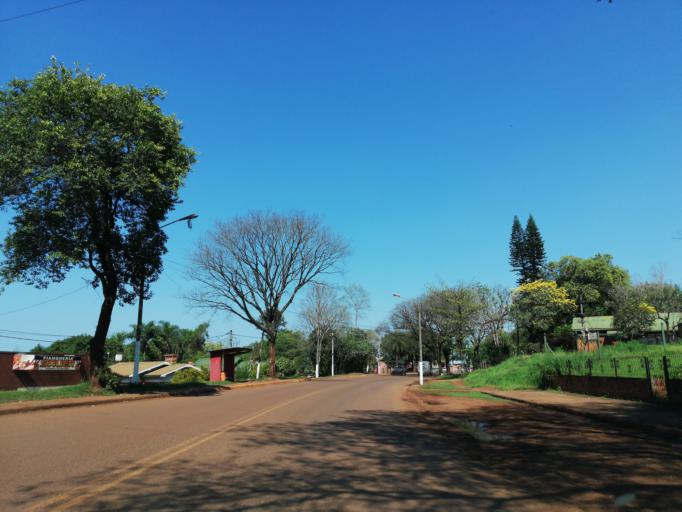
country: AR
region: Misiones
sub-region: Departamento de Eldorado
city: Eldorado
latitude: -26.4085
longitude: -54.6424
